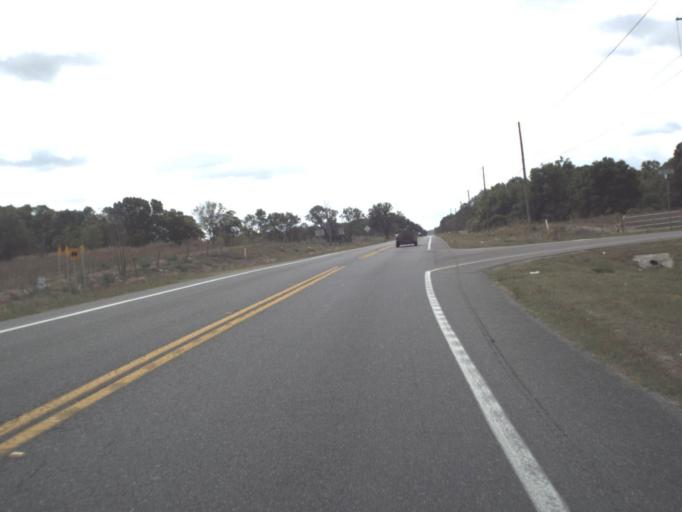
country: US
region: Florida
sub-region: Marion County
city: Ocala
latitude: 29.2580
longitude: -82.0729
